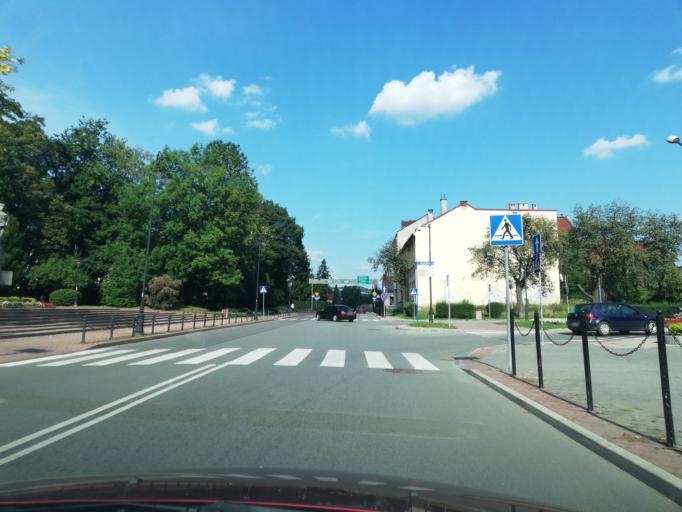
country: PL
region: Lesser Poland Voivodeship
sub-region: Powiat nowosadecki
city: Nowy Sacz
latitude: 49.6188
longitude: 20.6952
